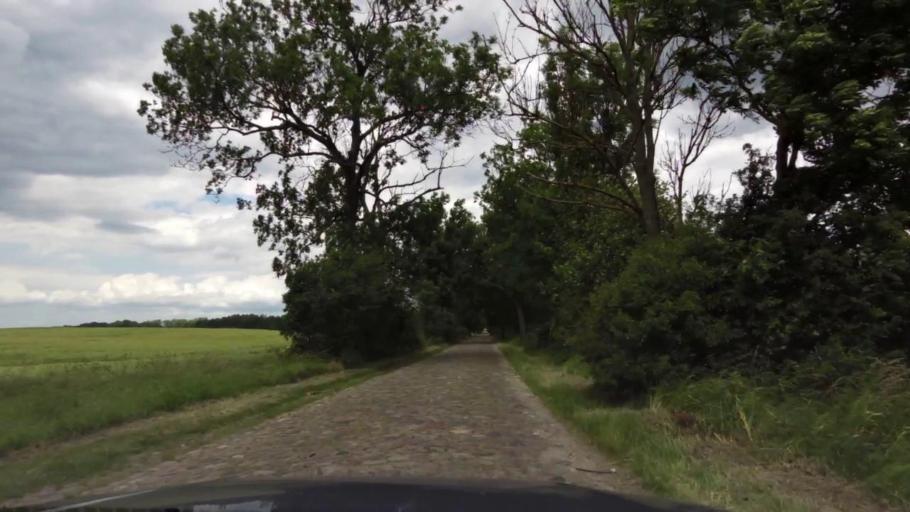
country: PL
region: West Pomeranian Voivodeship
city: Trzcinsko Zdroj
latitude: 52.9579
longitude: 14.7130
